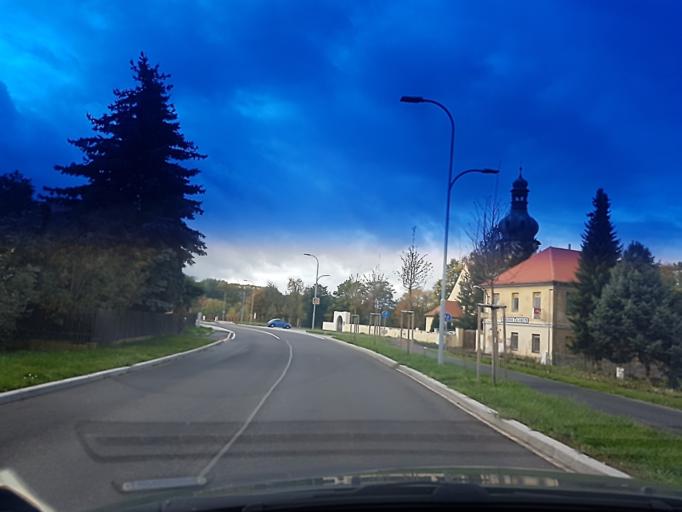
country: DE
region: Bavaria
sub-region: Upper Franconia
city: Schirnding
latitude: 50.0862
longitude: 12.2862
